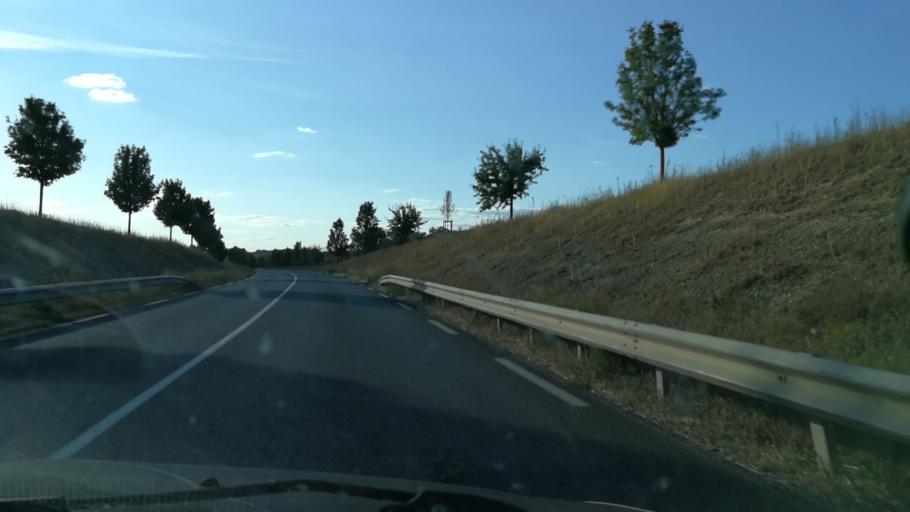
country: FR
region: Centre
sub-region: Departement d'Indre-et-Loire
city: Sainte-Maure-de-Touraine
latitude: 47.1041
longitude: 0.6034
